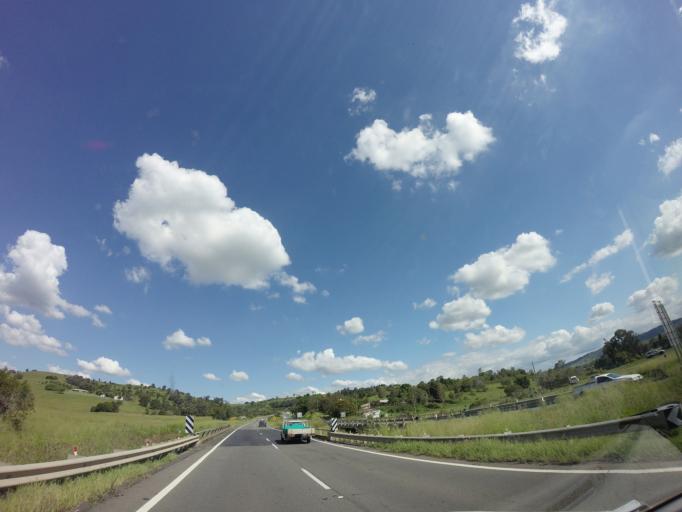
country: AU
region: Queensland
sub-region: Ipswich
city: Thagoona
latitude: -27.5580
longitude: 152.5490
